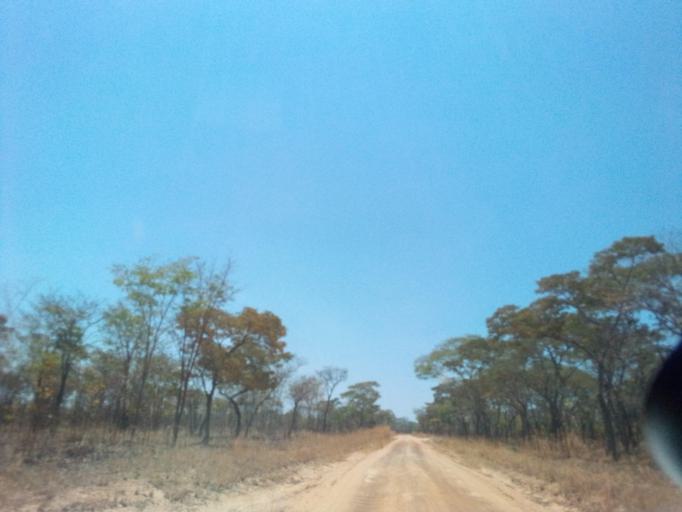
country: ZM
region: Northern
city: Mpika
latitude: -12.2532
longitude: 30.6963
